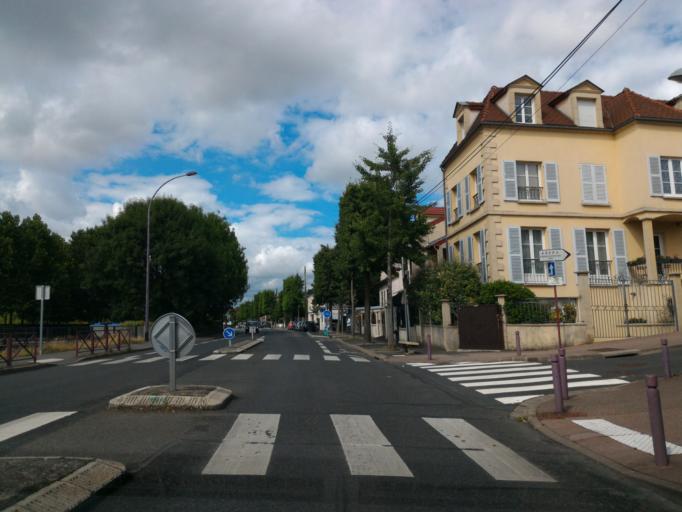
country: FR
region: Ile-de-France
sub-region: Departement des Hauts-de-Seine
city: Bourg-la-Reine
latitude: 48.7695
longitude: 2.3216
